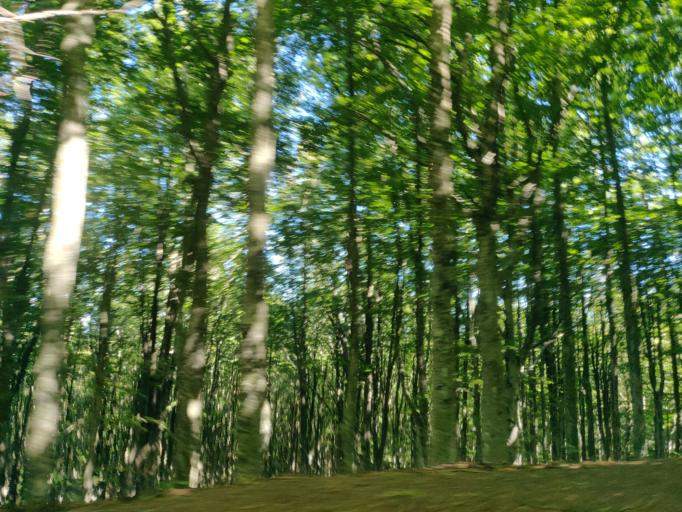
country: IT
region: Tuscany
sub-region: Provincia di Siena
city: Abbadia San Salvatore
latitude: 42.8944
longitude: 11.6326
